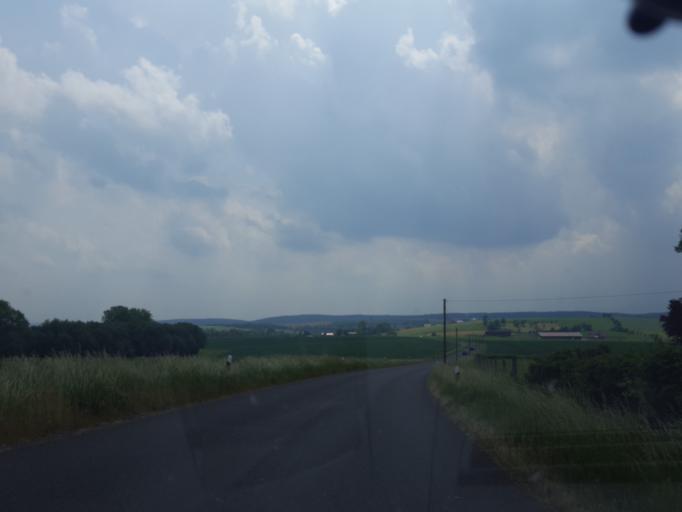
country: DE
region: Lower Saxony
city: Wollbrandshausen
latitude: 51.5797
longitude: 10.1574
